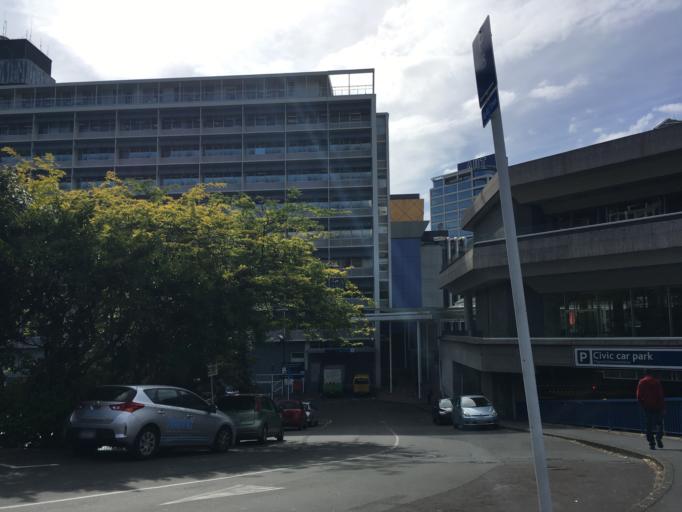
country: NZ
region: Auckland
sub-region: Auckland
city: Auckland
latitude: -36.8513
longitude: 174.7621
